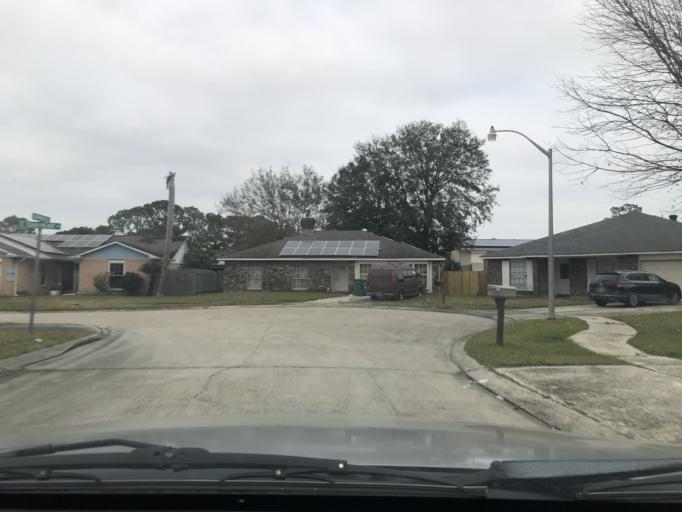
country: US
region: Louisiana
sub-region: Jefferson Parish
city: Woodmere
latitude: 29.8599
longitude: -90.0797
